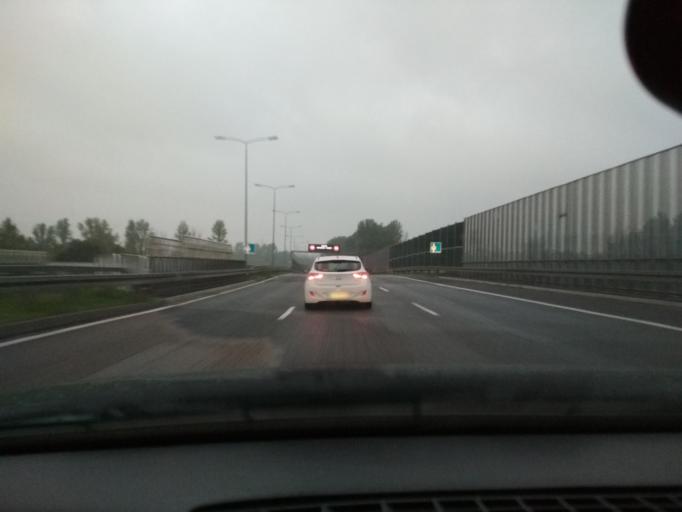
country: PL
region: Silesian Voivodeship
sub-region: Powiat gliwicki
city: Przyszowice
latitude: 50.2838
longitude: 18.7424
